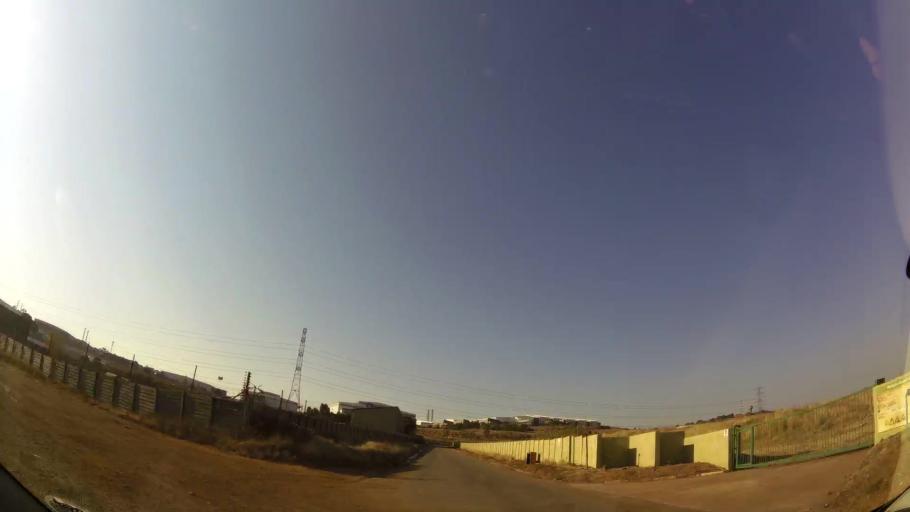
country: ZA
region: Gauteng
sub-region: City of Johannesburg Metropolitan Municipality
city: Modderfontein
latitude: -26.1564
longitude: 28.1763
